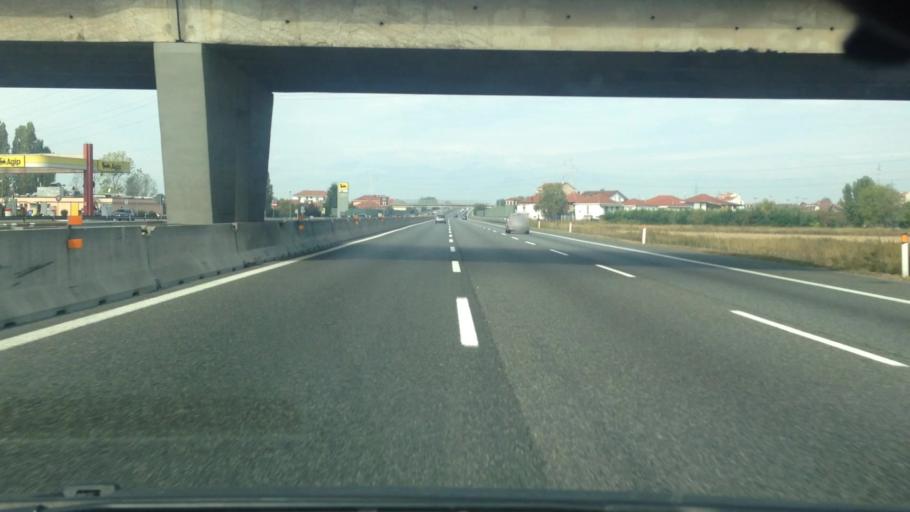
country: IT
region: Piedmont
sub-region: Provincia di Torino
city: Nichelino
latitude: 44.9809
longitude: 7.6469
